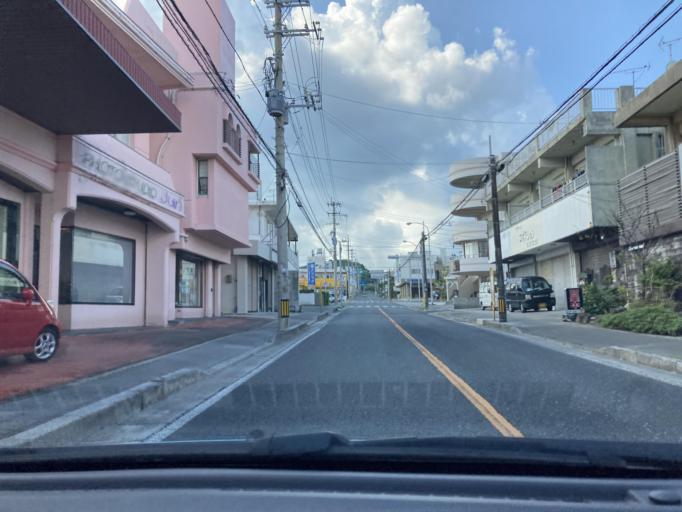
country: JP
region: Okinawa
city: Tomigusuku
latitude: 26.1766
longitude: 127.7186
